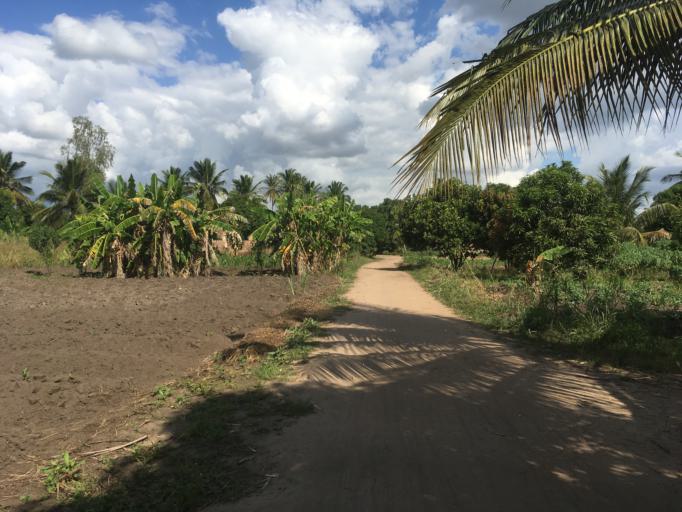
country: MZ
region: Zambezia
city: Quelimane
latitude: -17.6437
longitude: 36.6859
